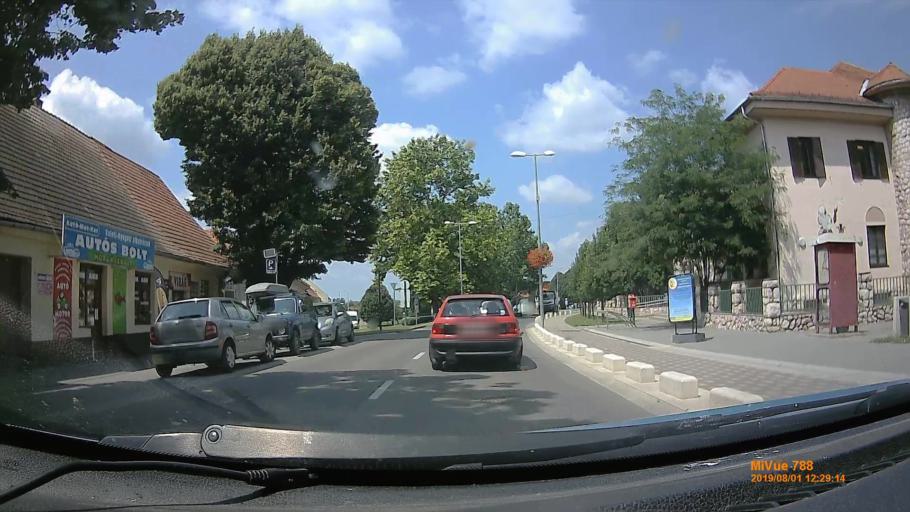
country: HU
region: Baranya
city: Siklos
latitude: 45.8554
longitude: 18.2959
